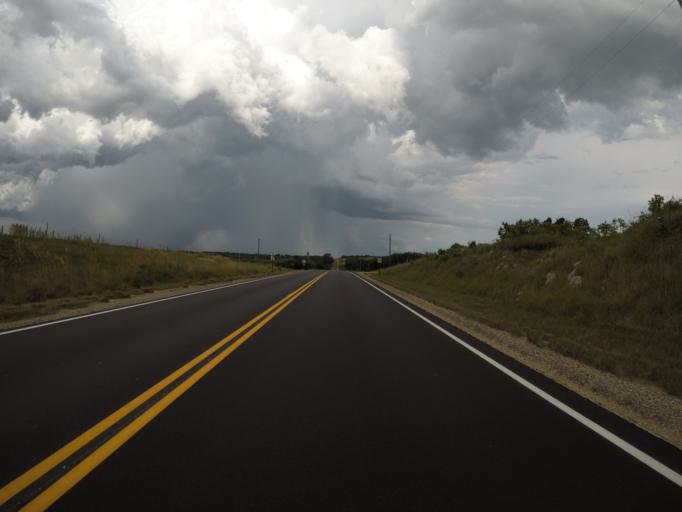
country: US
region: Kansas
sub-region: Clay County
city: Clay Center
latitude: 39.4369
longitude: -96.8352
